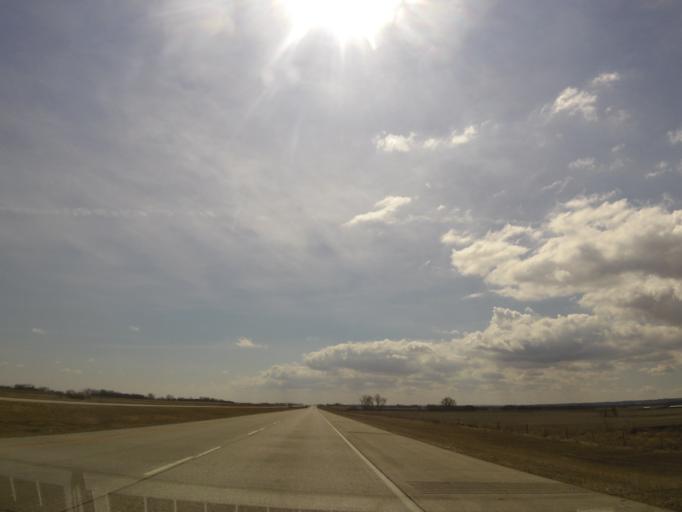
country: US
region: South Dakota
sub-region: Roberts County
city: Sisseton
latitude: 45.5698
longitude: -96.9897
